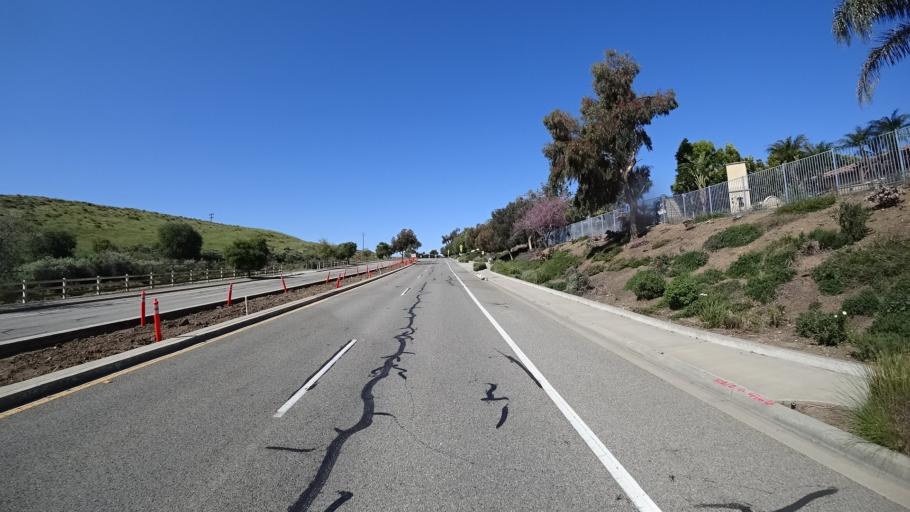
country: US
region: California
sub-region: Ventura County
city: Casa Conejo
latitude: 34.1579
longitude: -118.9715
